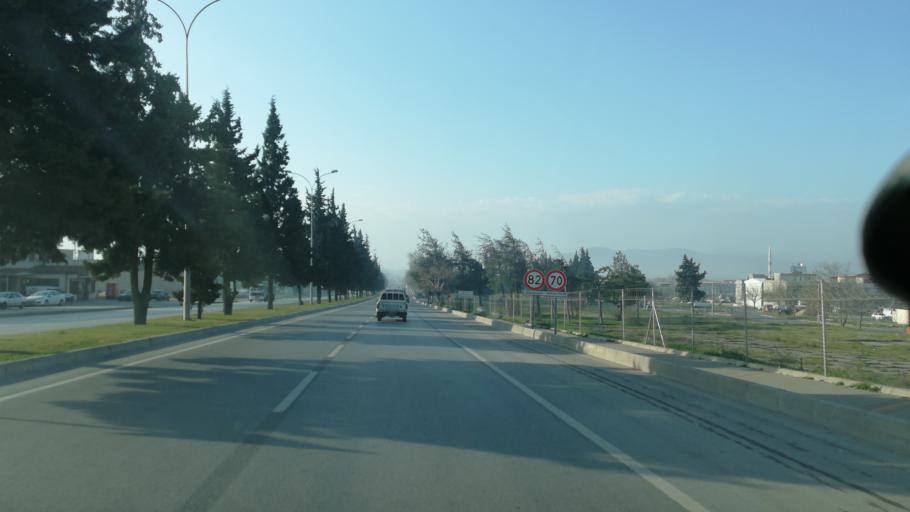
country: TR
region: Kahramanmaras
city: Kahramanmaras
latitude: 37.5653
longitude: 36.9241
